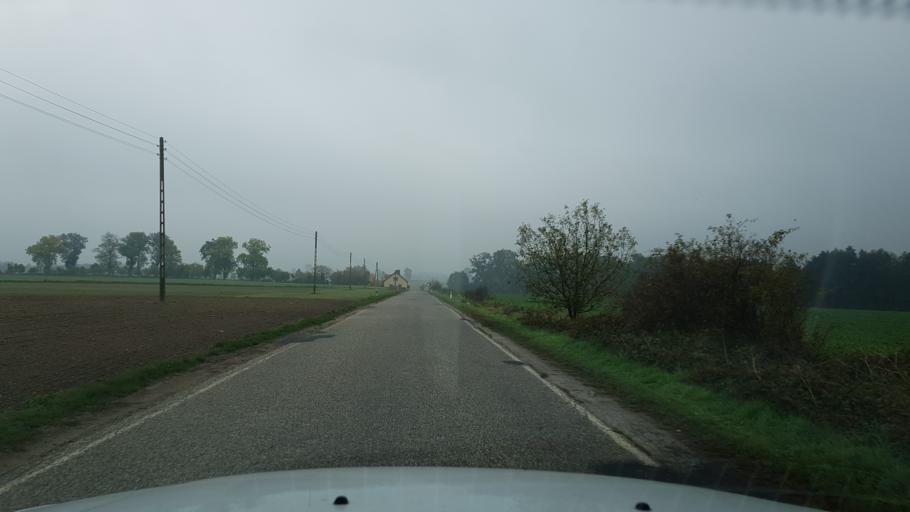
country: PL
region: West Pomeranian Voivodeship
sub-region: Powiat stargardzki
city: Dolice
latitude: 53.1595
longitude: 15.2358
